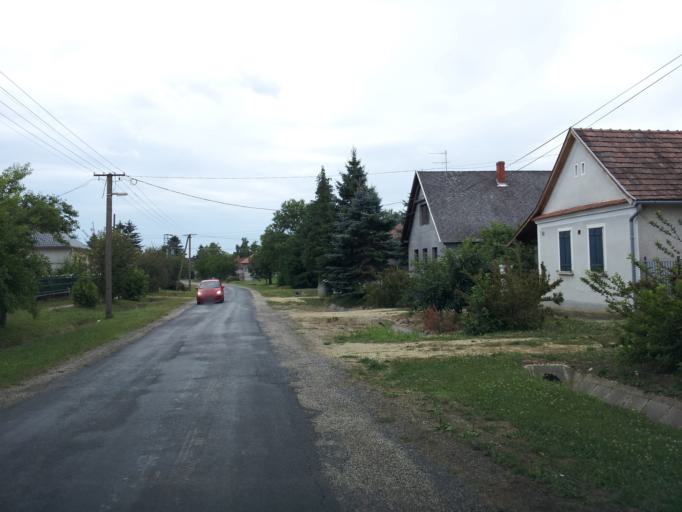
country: HU
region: Vas
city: Vasvar
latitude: 47.0508
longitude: 16.8729
